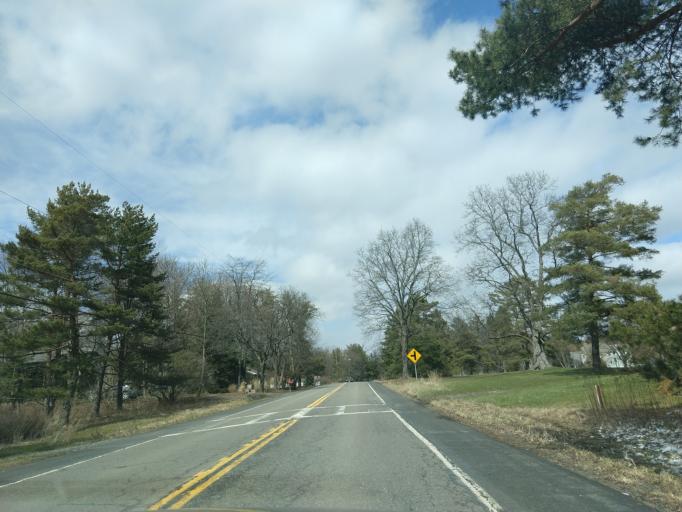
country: US
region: New York
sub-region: Tompkins County
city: Northeast Ithaca
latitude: 42.4643
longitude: -76.4670
